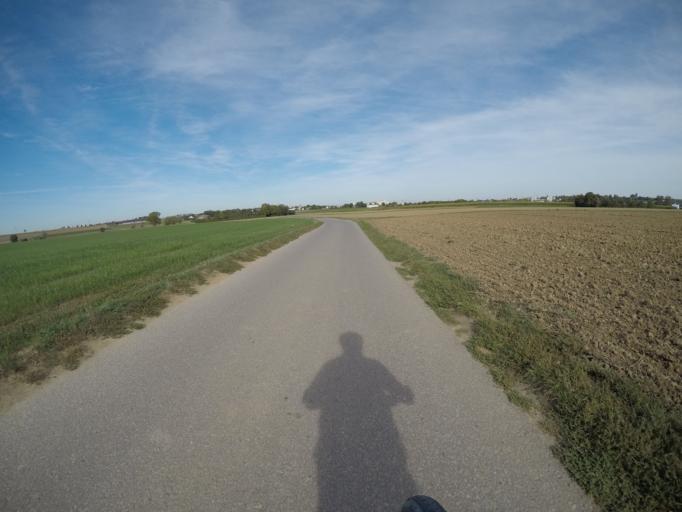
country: DE
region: Baden-Wuerttemberg
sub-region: Regierungsbezirk Stuttgart
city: Korntal
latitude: 48.8449
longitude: 9.1066
